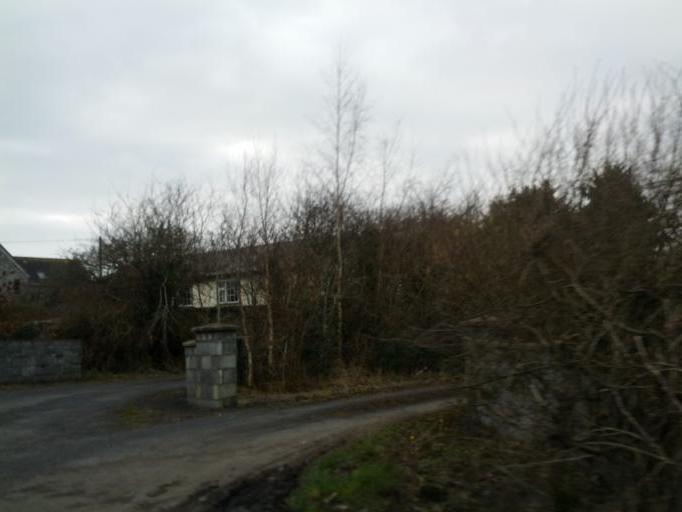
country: IE
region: Connaught
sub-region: County Galway
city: Oranmore
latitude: 53.2223
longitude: -8.8850
